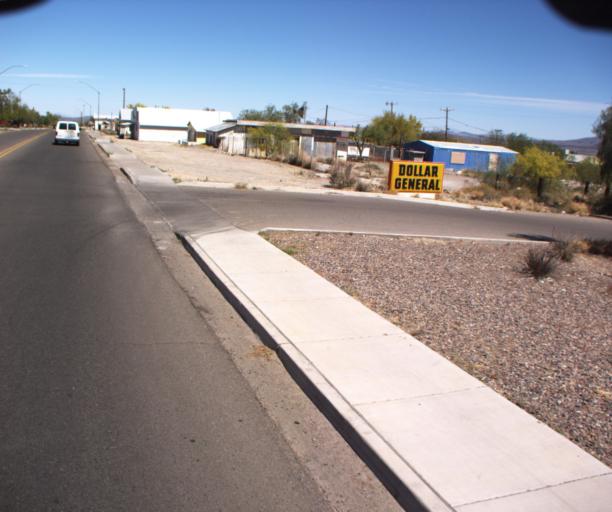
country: US
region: Arizona
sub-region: Pima County
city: Ajo
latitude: 32.3795
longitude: -112.8724
